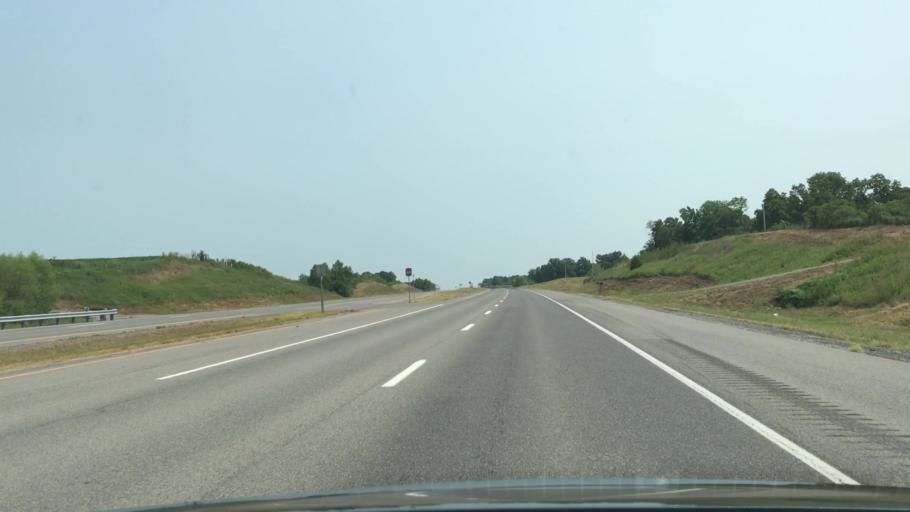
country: US
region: Kentucky
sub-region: Calloway County
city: Murray
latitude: 36.7355
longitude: -88.1691
